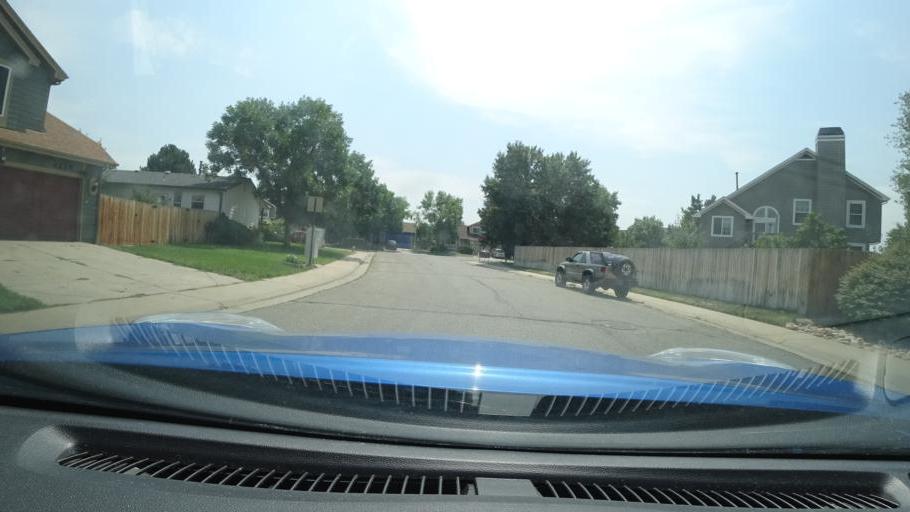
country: US
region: Colorado
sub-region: Adams County
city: Aurora
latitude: 39.7749
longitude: -104.7567
